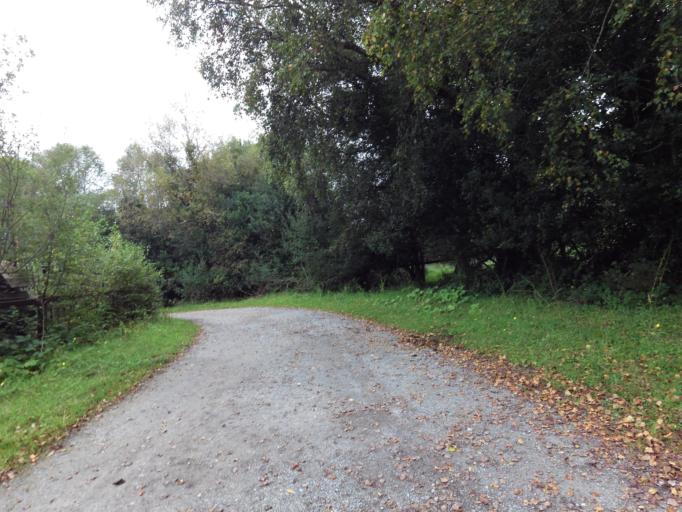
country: IE
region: Connaught
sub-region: County Galway
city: Loughrea
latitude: 53.1313
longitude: -8.4800
